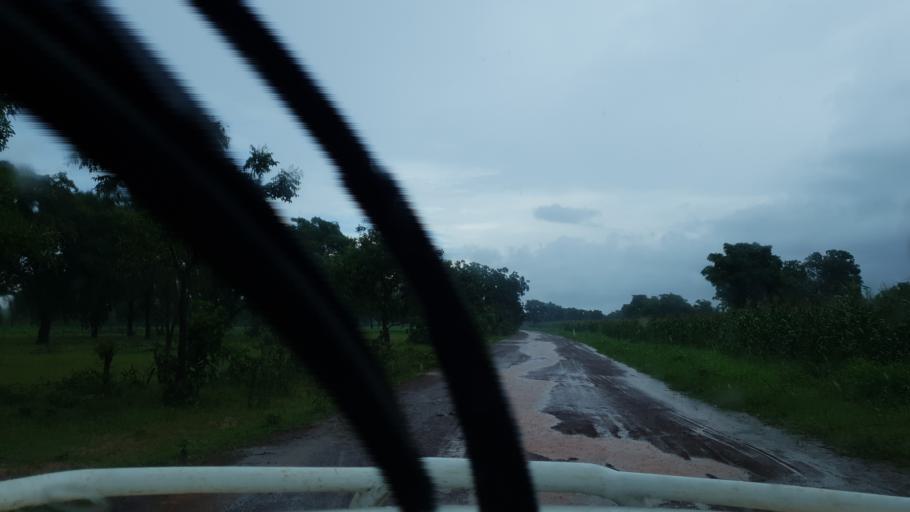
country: ML
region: Sikasso
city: Kolondieba
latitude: 11.5988
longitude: -6.6678
